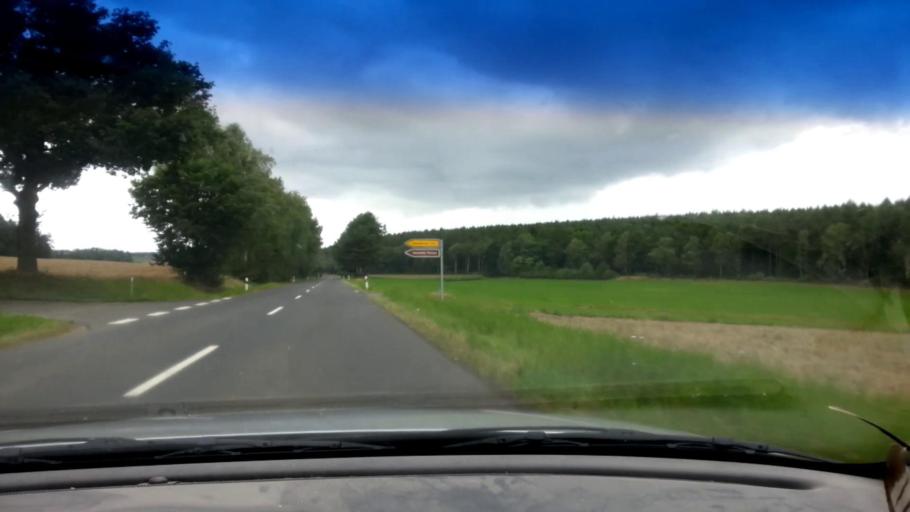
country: DE
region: Bavaria
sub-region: Upper Palatinate
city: Waldsassen
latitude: 50.0302
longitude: 12.3157
